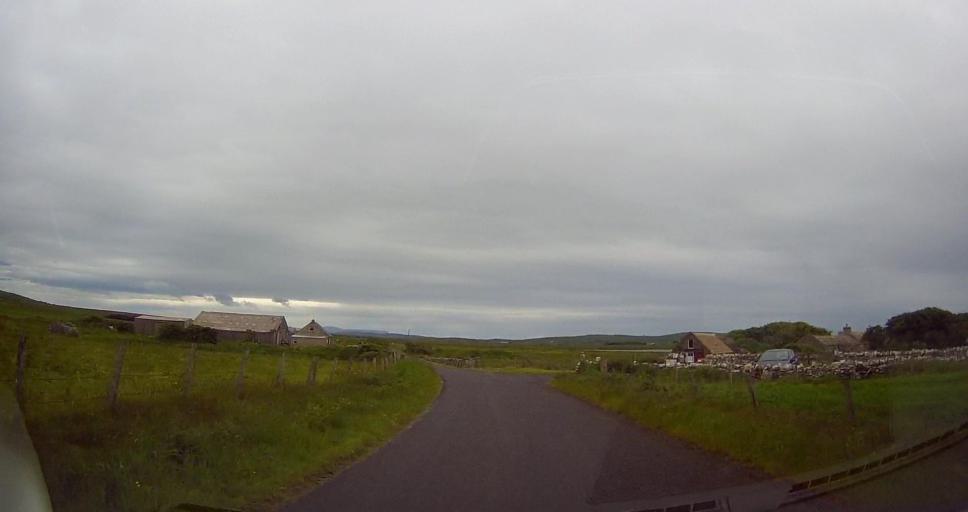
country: GB
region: Scotland
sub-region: Orkney Islands
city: Stromness
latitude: 59.1102
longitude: -3.2523
